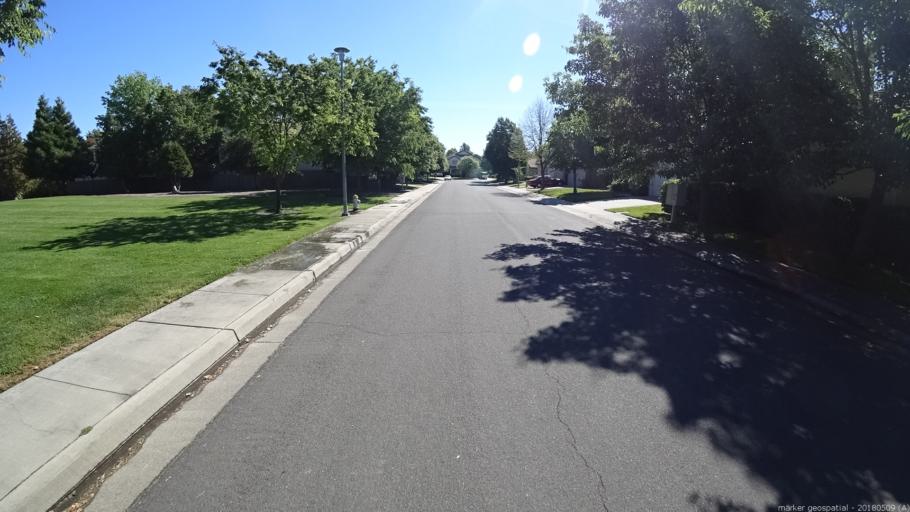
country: US
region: California
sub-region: Sacramento County
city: Elverta
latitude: 38.6710
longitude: -121.5206
